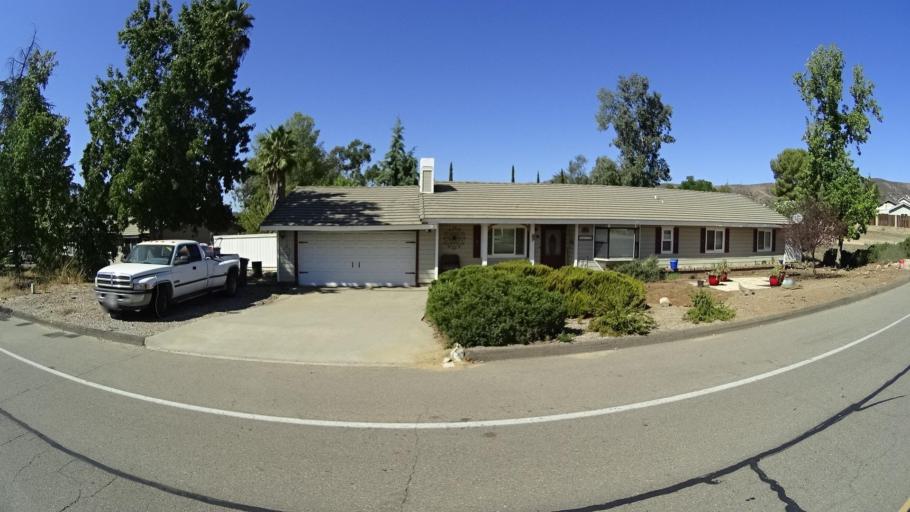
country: US
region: California
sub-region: San Diego County
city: San Diego Country Estates
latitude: 33.0116
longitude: -116.8125
